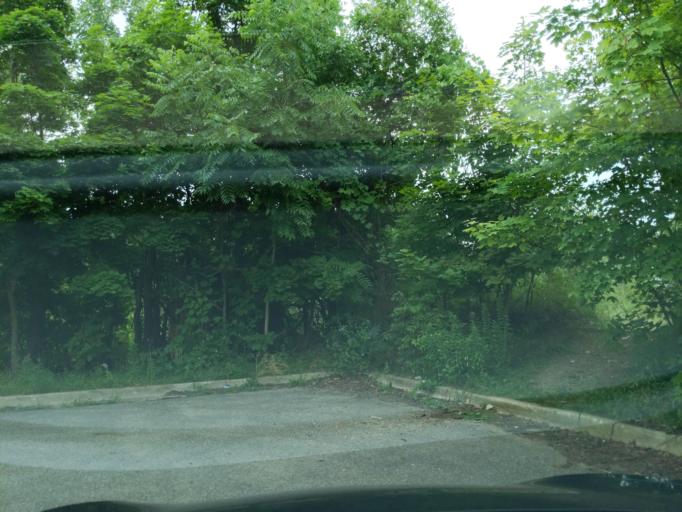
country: US
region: Michigan
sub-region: Ingham County
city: Lansing
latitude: 42.7622
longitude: -84.5377
